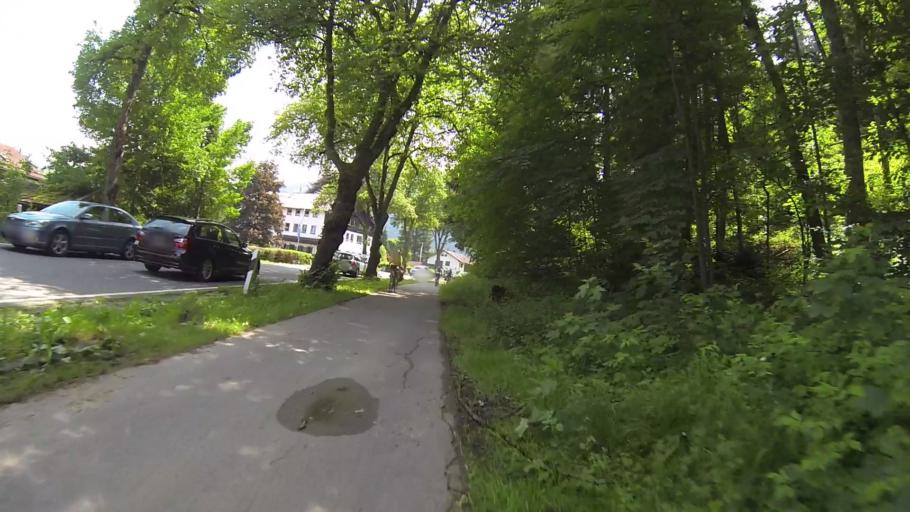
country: DE
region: Bavaria
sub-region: Swabia
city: Schwangau
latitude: 47.5656
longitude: 10.7250
